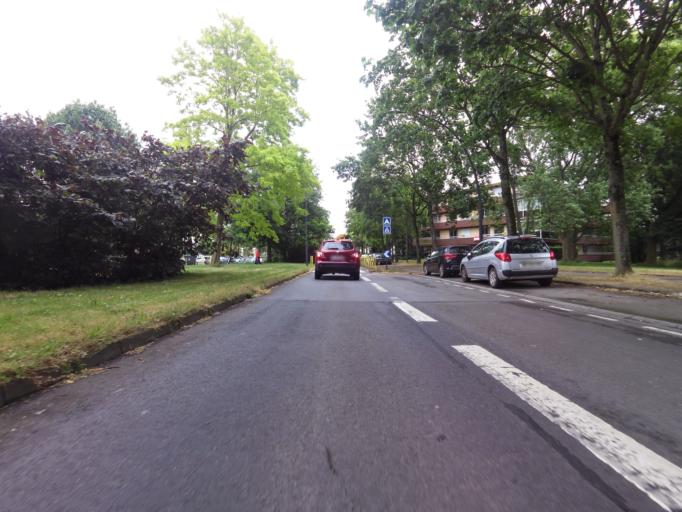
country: FR
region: Brittany
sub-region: Departement d'Ille-et-Vilaine
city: Rennes
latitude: 48.0836
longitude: -1.6695
